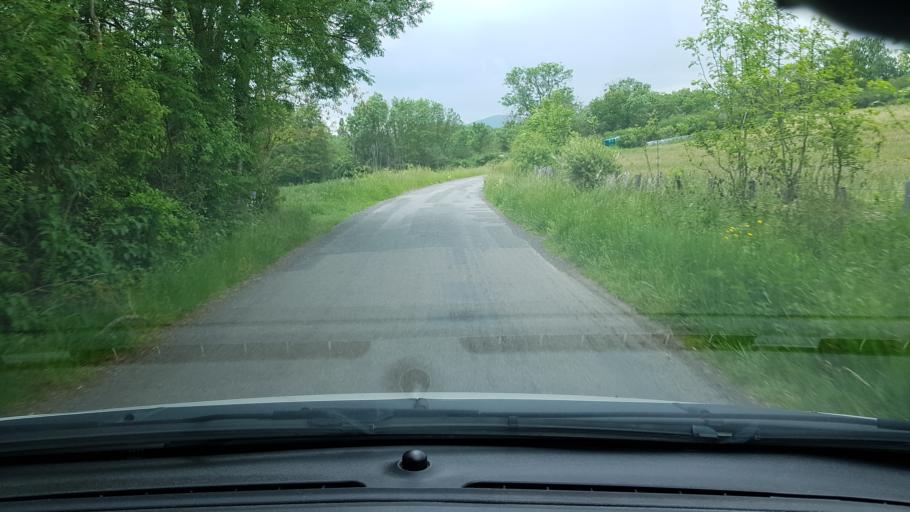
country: FR
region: Rhone-Alpes
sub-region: Departement du Rhone
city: Chassagny
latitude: 45.6051
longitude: 4.7133
